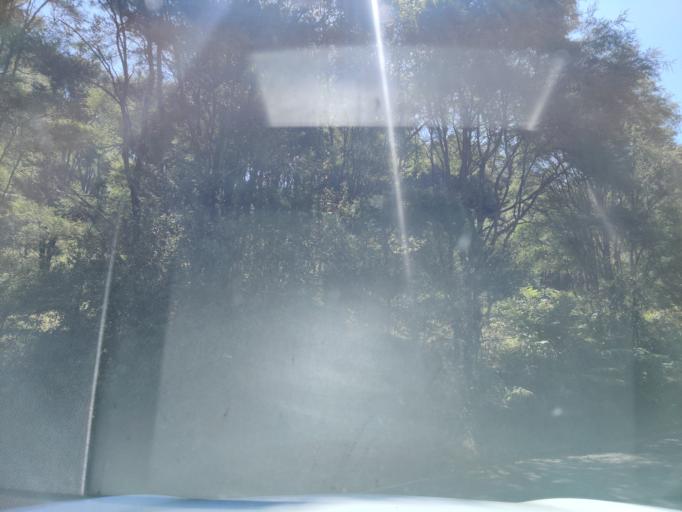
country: NZ
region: Auckland
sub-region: Auckland
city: Red Hill
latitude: -37.0668
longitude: 175.0891
